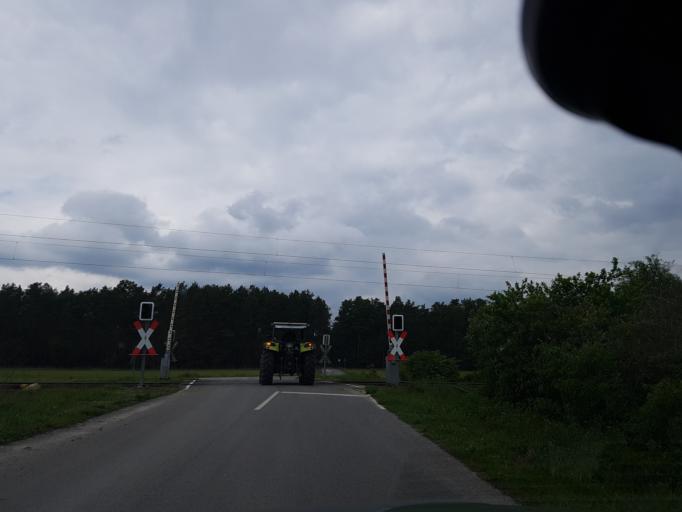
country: DE
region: Brandenburg
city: Crinitz
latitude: 51.6627
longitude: 13.7850
